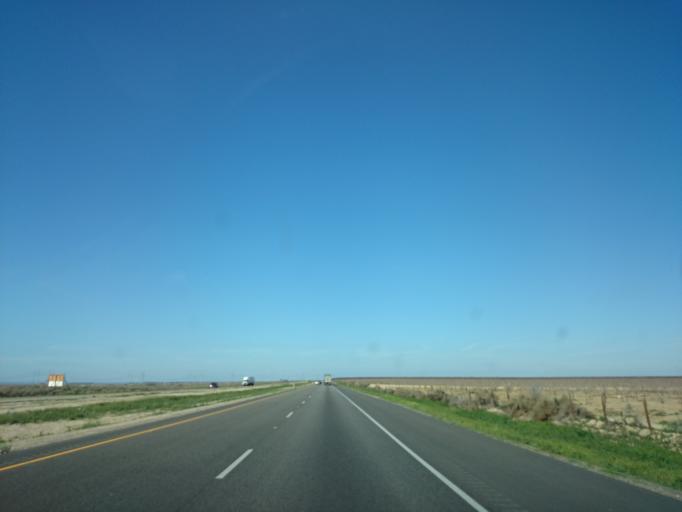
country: US
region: California
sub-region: Kern County
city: Buttonwillow
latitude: 35.4699
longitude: -119.4945
